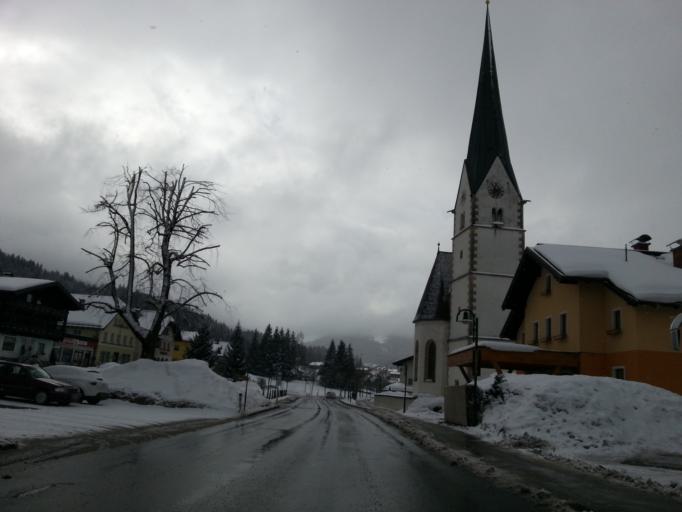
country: AT
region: Salzburg
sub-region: Politischer Bezirk Sankt Johann im Pongau
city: Eben im Pongau
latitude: 47.4653
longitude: 13.3810
